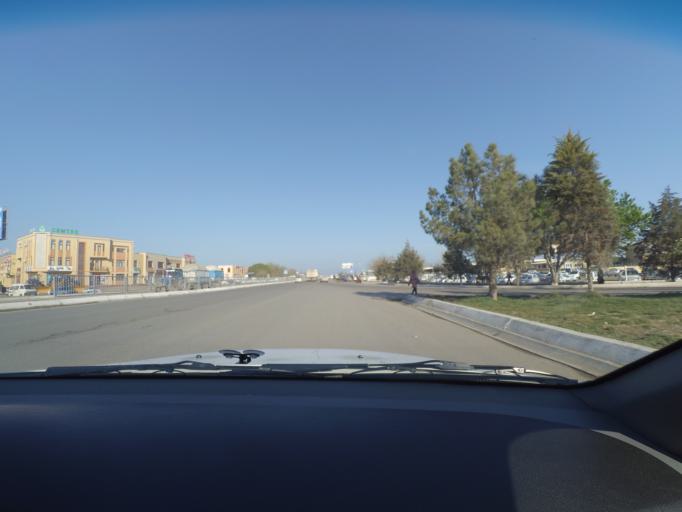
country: UZ
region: Bukhara
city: Bukhara
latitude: 39.8037
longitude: 64.4271
